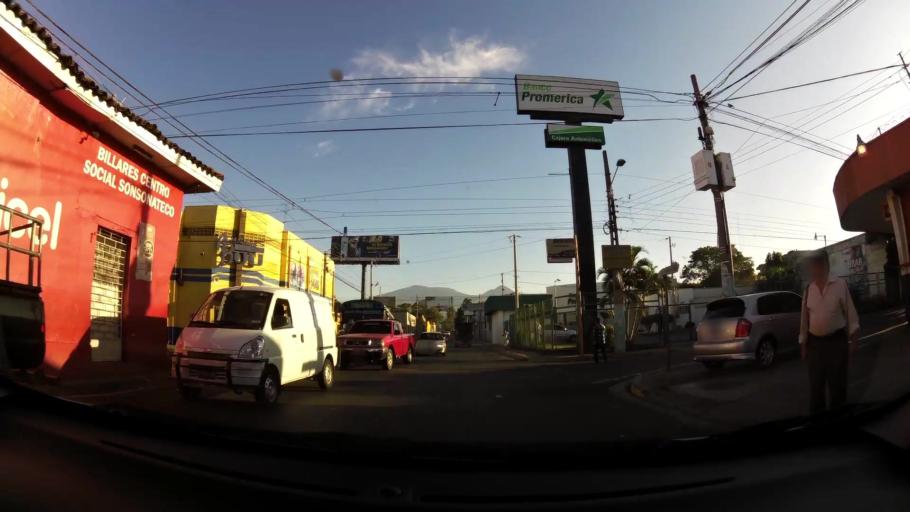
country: SV
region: Sonsonate
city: Sonsonate
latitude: 13.7185
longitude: -89.7221
